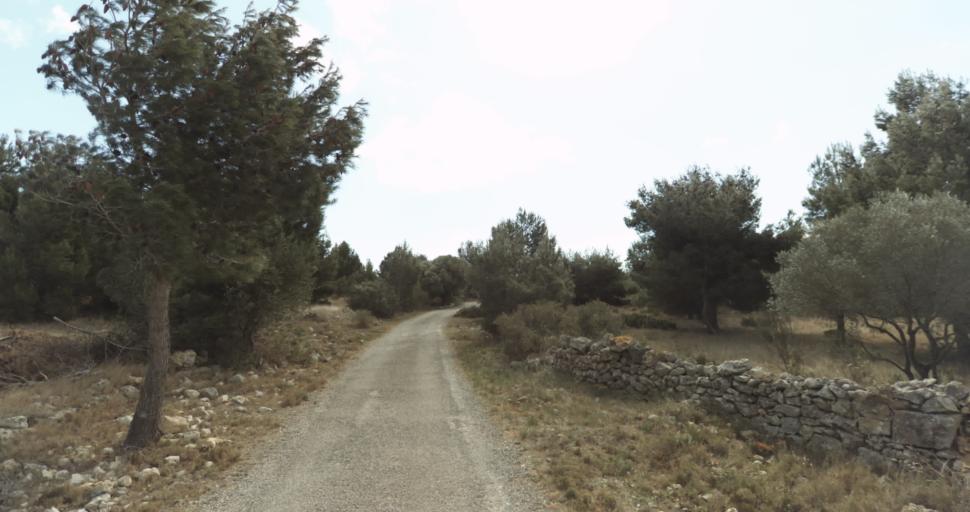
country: FR
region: Languedoc-Roussillon
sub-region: Departement de l'Aude
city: Leucate
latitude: 42.9191
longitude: 3.0490
